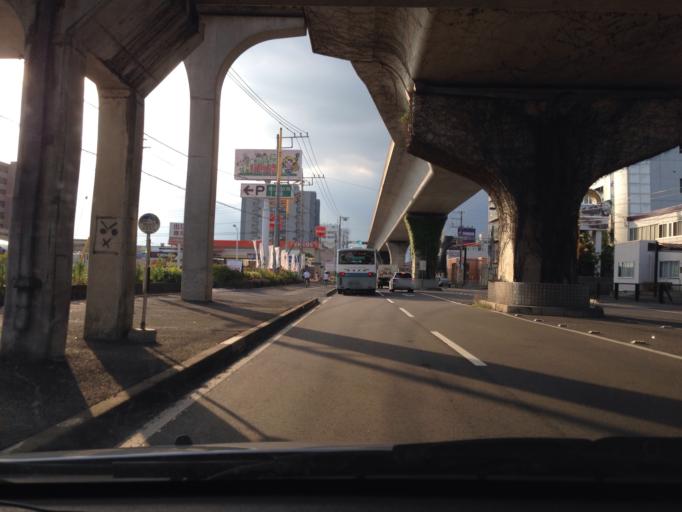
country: JP
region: Ibaraki
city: Naka
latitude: 36.0846
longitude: 140.1893
